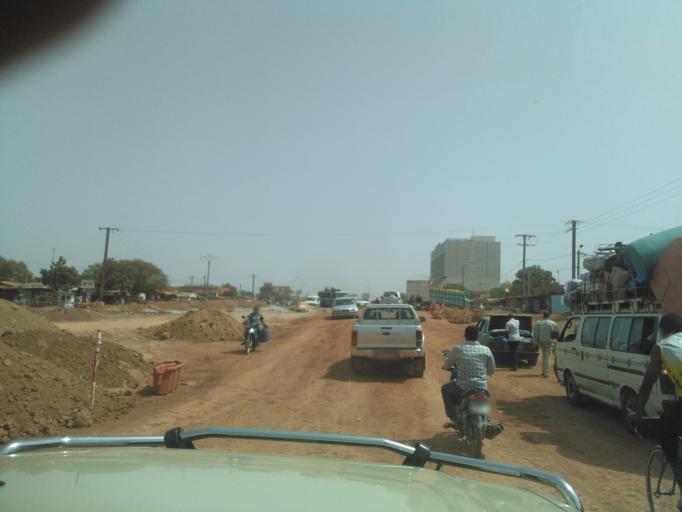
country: BF
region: Centre
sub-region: Kadiogo Province
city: Ouagadougou
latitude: 12.3911
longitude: -1.4761
